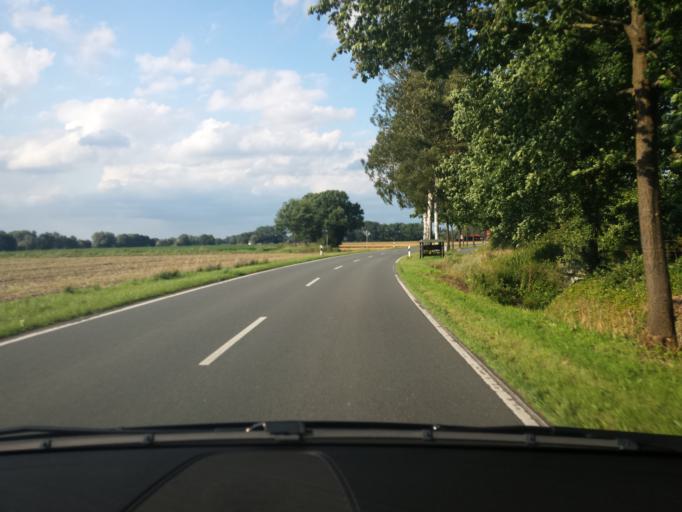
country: DE
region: North Rhine-Westphalia
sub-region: Regierungsbezirk Arnsberg
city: Lippstadt
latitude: 51.6899
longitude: 8.3000
